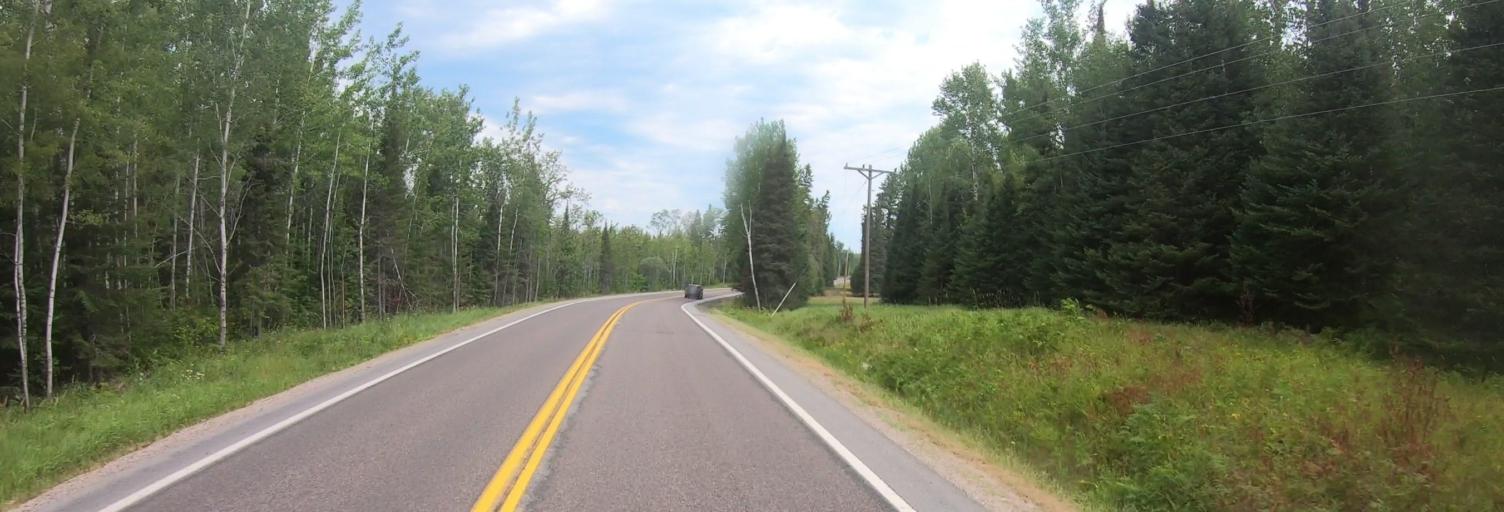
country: US
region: Minnesota
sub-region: Saint Louis County
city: Mountain Iron
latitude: 47.9052
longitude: -92.6582
